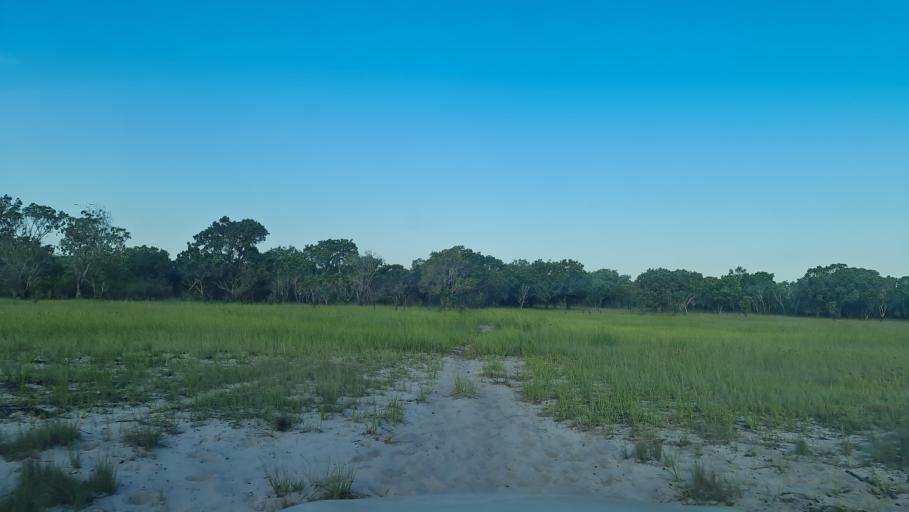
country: MZ
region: Gaza
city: Macia
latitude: -25.2268
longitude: 33.0232
